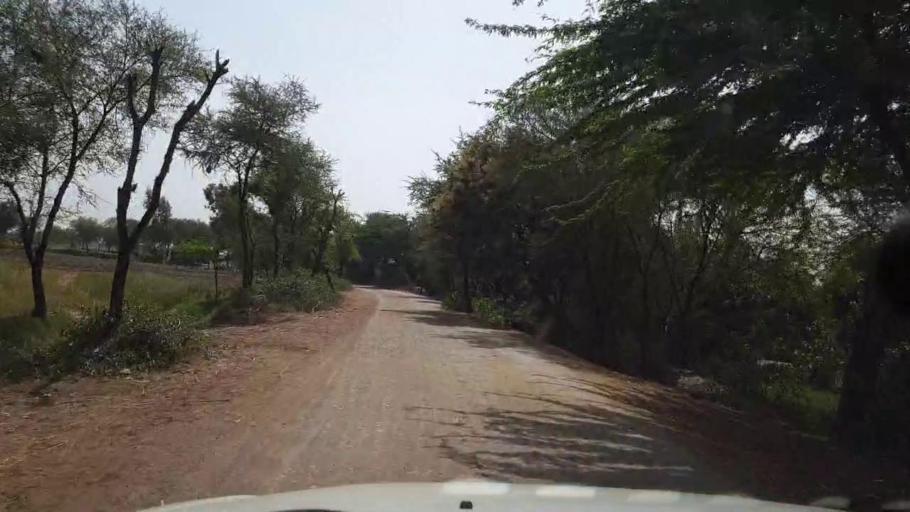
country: PK
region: Sindh
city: Matli
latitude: 25.0267
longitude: 68.7051
